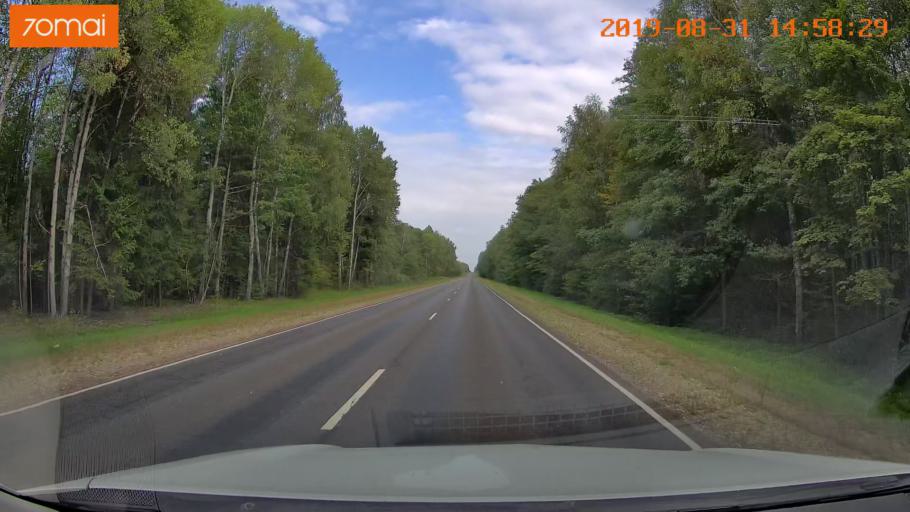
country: RU
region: Kaluga
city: Spas-Demensk
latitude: 54.3179
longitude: 33.9827
